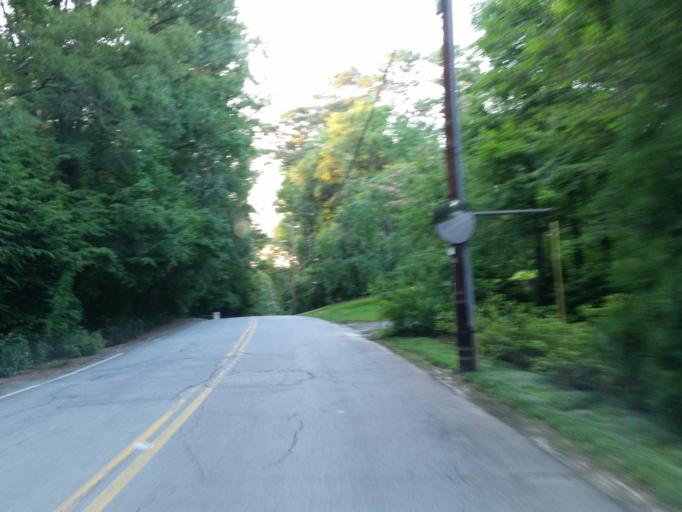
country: US
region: Georgia
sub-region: Cobb County
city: Vinings
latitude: 33.8738
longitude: -84.4343
